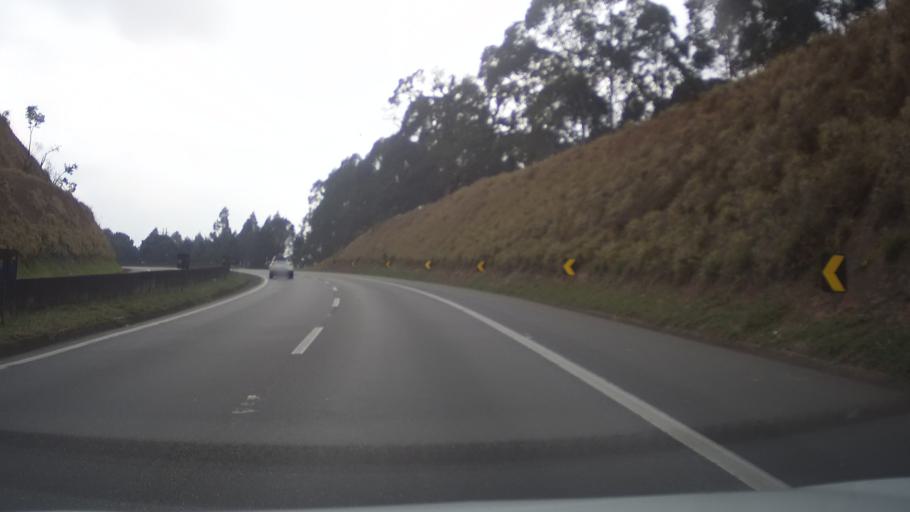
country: BR
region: Minas Gerais
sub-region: Extrema
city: Extrema
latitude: -22.8588
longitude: -46.3383
